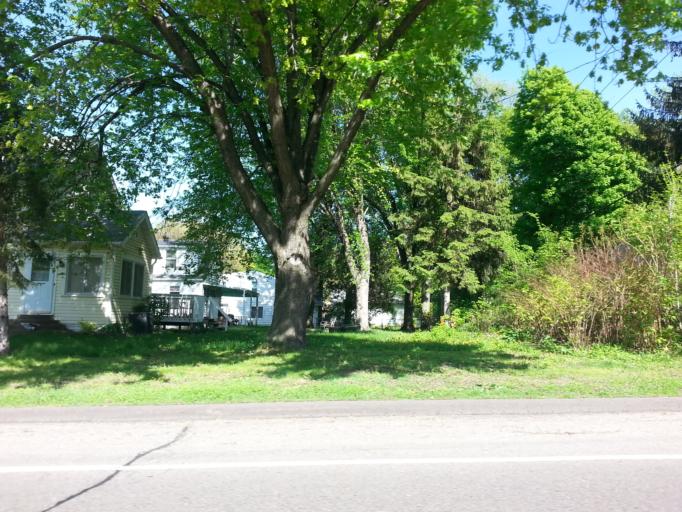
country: US
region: Minnesota
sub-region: Ramsey County
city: North Saint Paul
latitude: 45.0137
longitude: -92.9848
